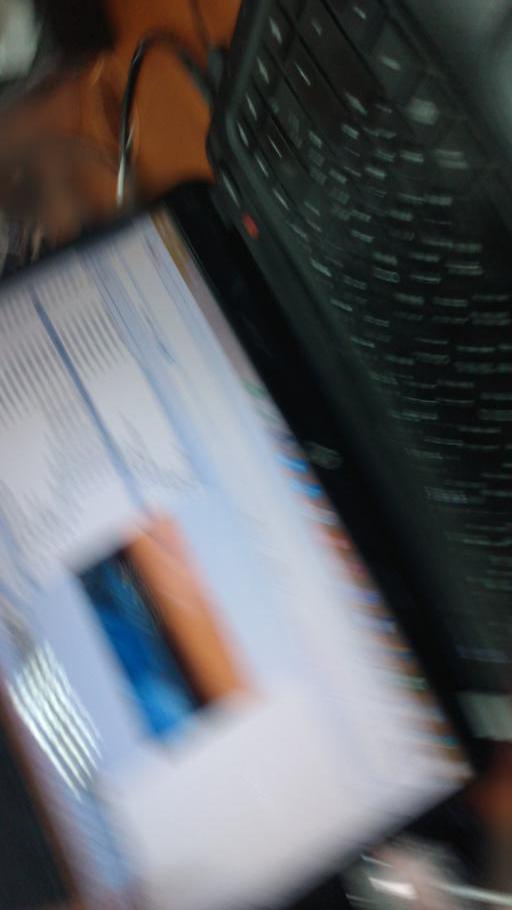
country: RU
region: Moskovskaya
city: Mamontovka
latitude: 55.9860
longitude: 37.8107
